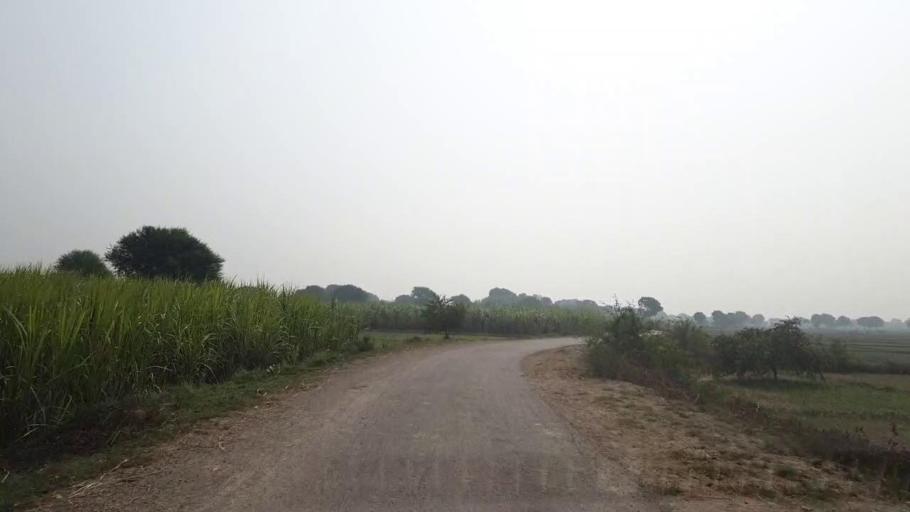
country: PK
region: Sindh
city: Tando Muhammad Khan
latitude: 25.1904
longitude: 68.6254
